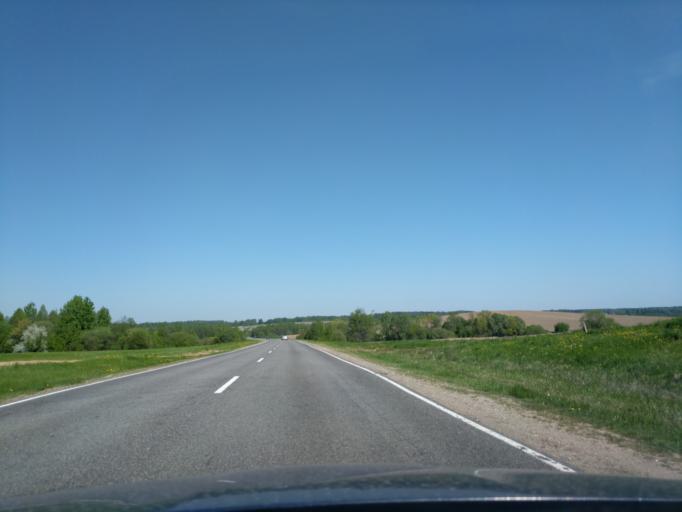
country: BY
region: Minsk
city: Il'ya
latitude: 54.2921
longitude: 27.4842
